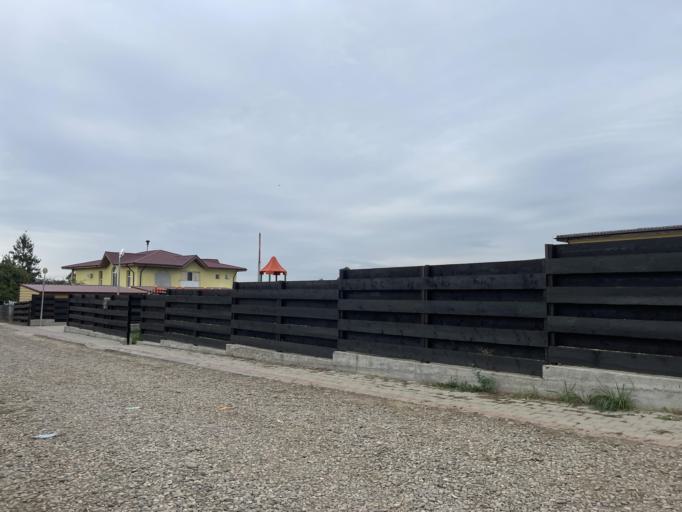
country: RO
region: Iasi
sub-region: Comuna Dumesti
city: Dumesti
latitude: 47.1718
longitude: 27.3379
